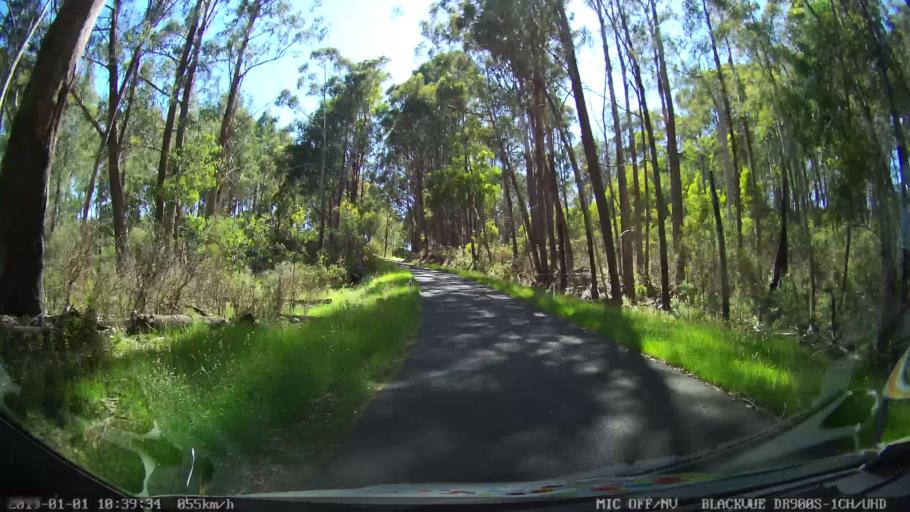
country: AU
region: New South Wales
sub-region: Snowy River
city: Jindabyne
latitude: -36.0400
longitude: 148.3056
